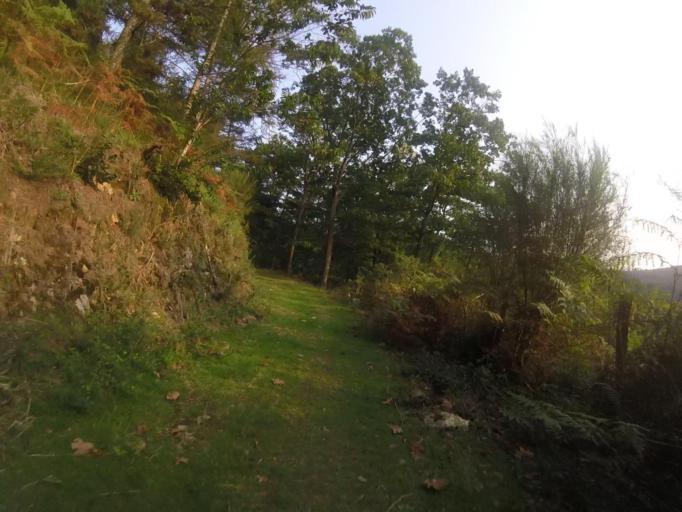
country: ES
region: Navarre
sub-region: Provincia de Navarra
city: Arano
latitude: 43.2535
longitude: -1.8355
